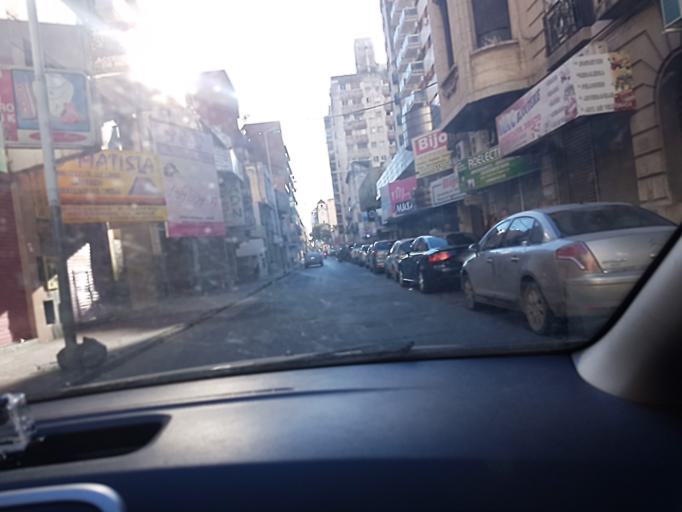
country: AR
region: Cordoba
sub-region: Departamento de Capital
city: Cordoba
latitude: -31.4198
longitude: -64.1843
